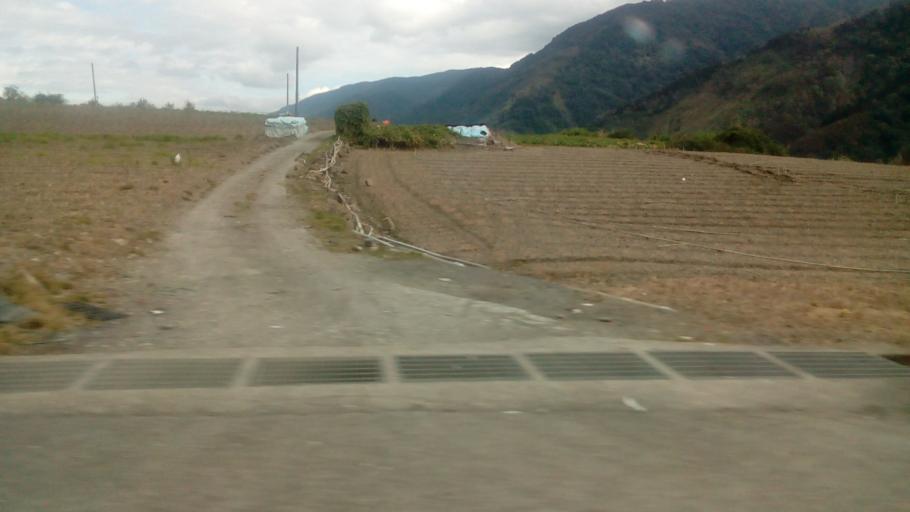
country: TW
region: Taiwan
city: Daxi
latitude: 24.4584
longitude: 121.3943
